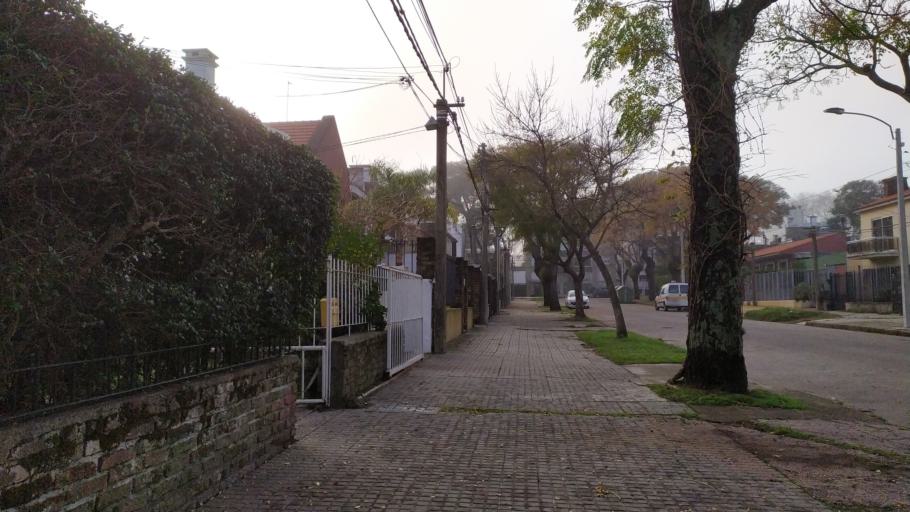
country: UY
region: Canelones
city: Paso de Carrasco
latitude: -34.8928
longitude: -56.0978
